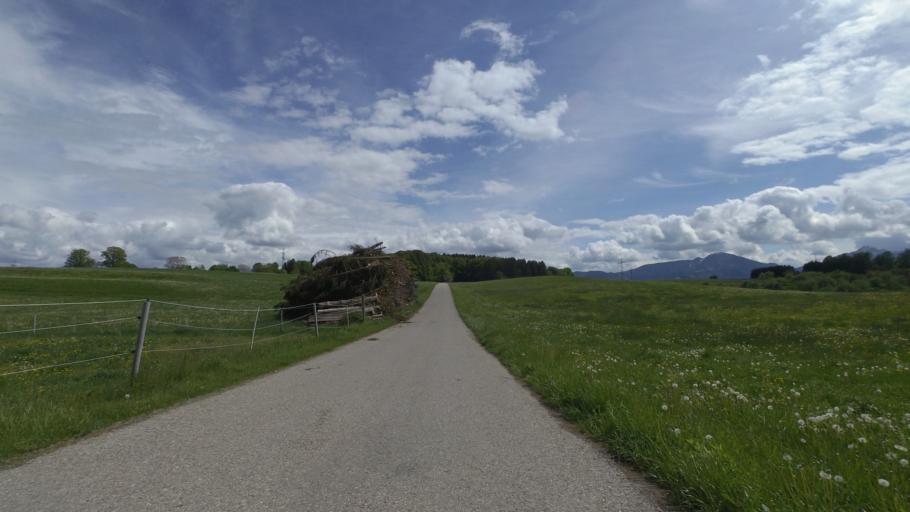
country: DE
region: Bavaria
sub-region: Upper Bavaria
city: Grabenstatt
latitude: 47.8620
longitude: 12.5775
